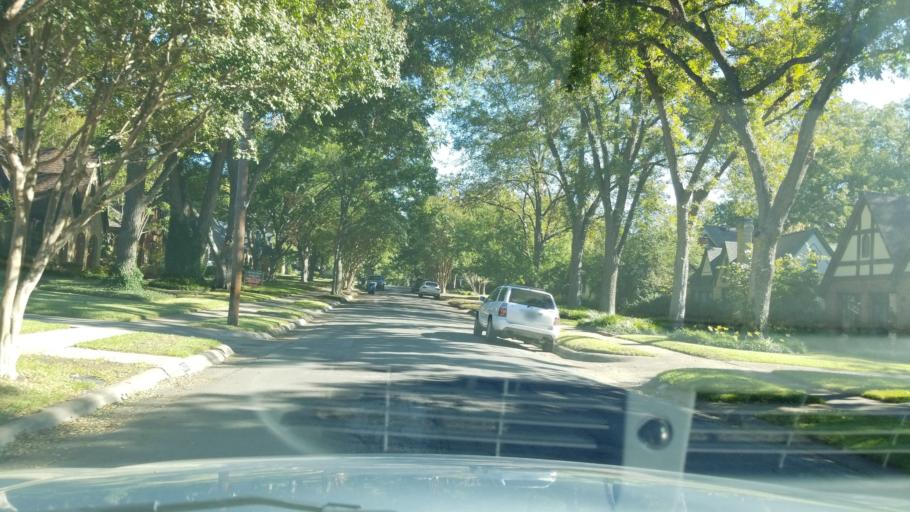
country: US
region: Texas
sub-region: Dallas County
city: Highland Park
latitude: 32.8050
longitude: -96.7464
